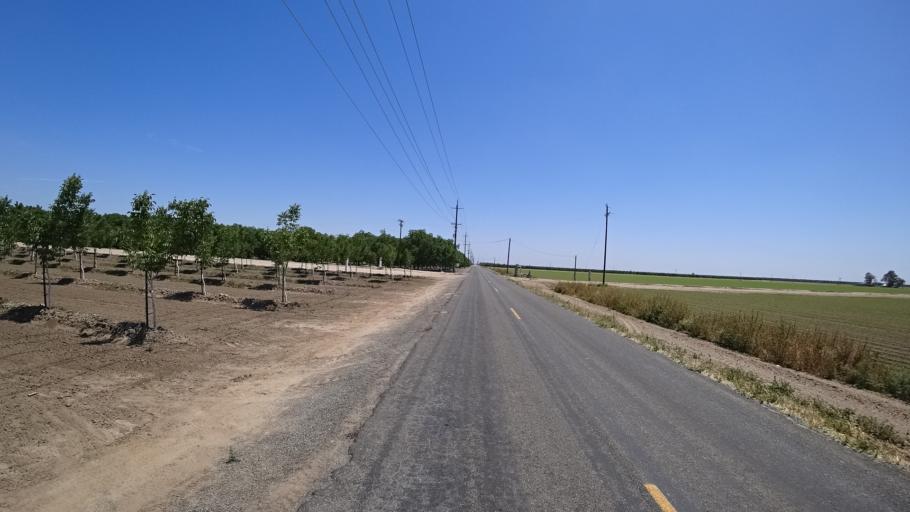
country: US
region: California
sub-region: Kings County
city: Armona
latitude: 36.2402
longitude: -119.7137
